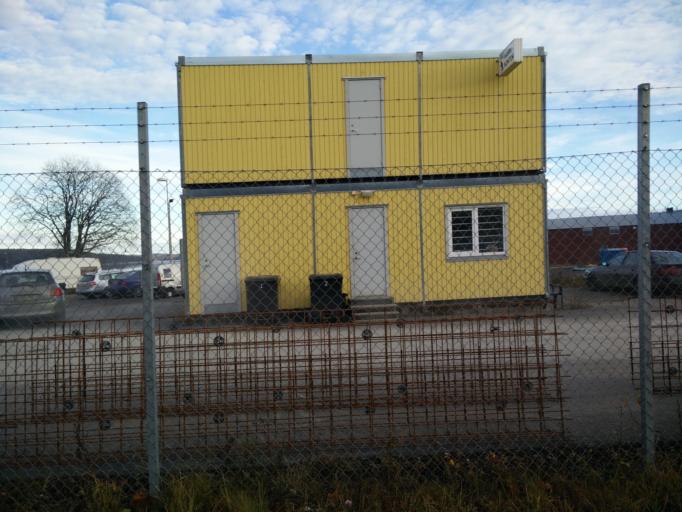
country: SE
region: Vaesternorrland
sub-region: Haernoesands Kommun
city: Haernoesand
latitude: 62.6429
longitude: 17.9346
